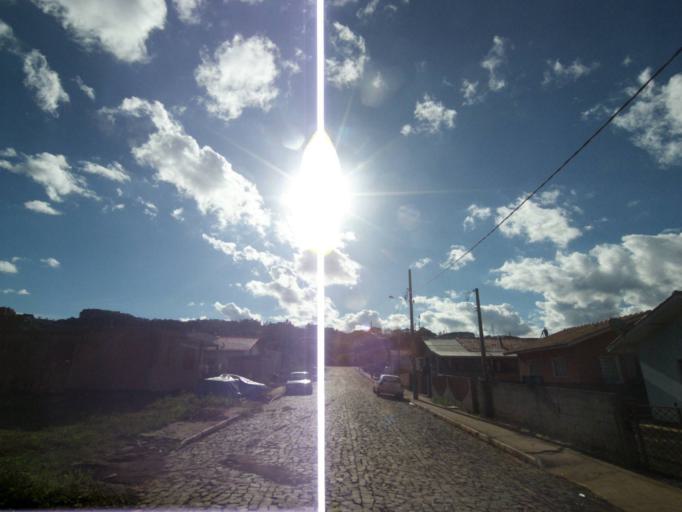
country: BR
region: Parana
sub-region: Uniao Da Vitoria
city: Uniao da Vitoria
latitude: -26.1622
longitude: -51.5323
